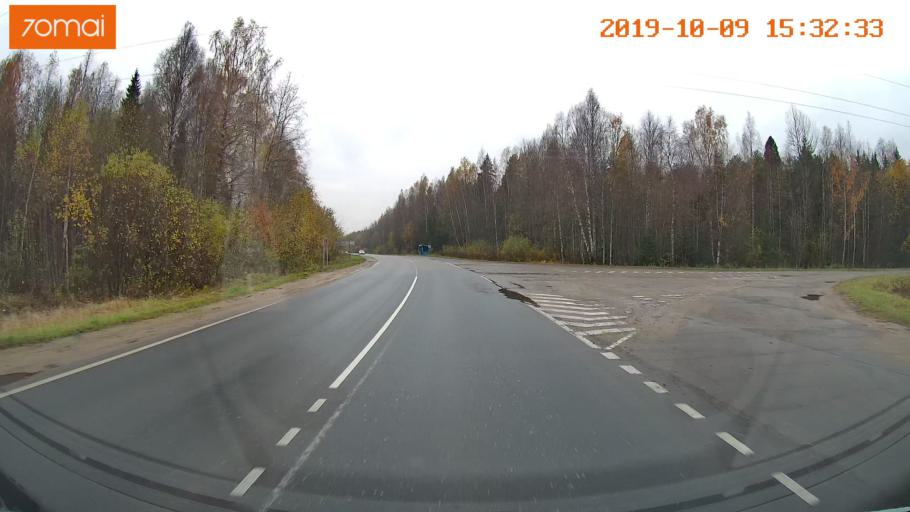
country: RU
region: Kostroma
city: Oktyabr'skiy
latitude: 57.9636
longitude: 41.2743
